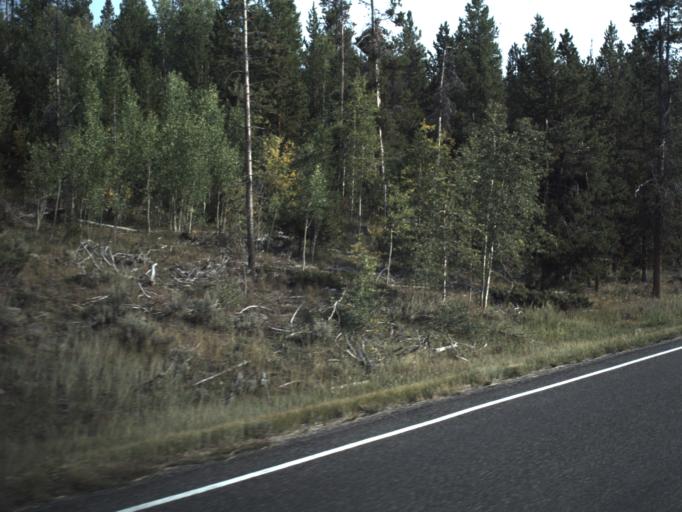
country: US
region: Wyoming
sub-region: Uinta County
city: Evanston
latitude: 40.8875
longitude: -110.8316
